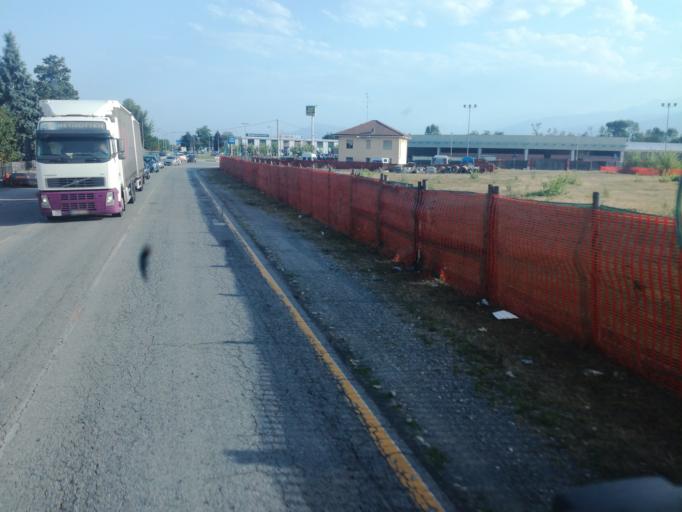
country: IT
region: Piedmont
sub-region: Provincia di Torino
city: Osasco
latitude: 44.8562
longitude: 7.3362
